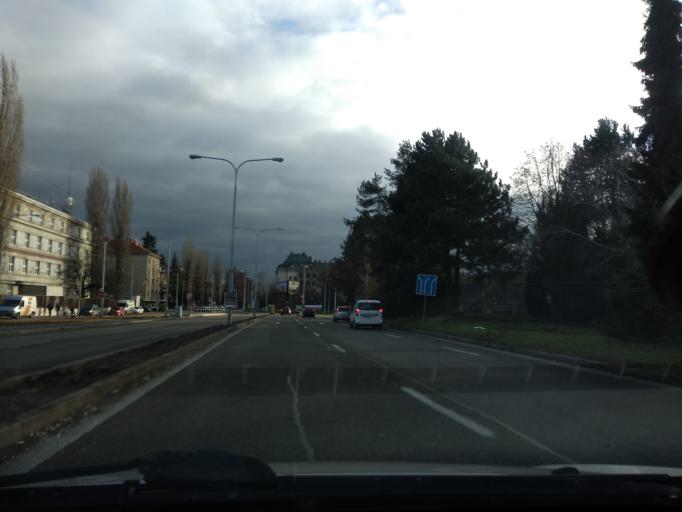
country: CZ
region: South Moravian
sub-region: Mesto Brno
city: Brno
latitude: 49.2139
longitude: 16.6164
